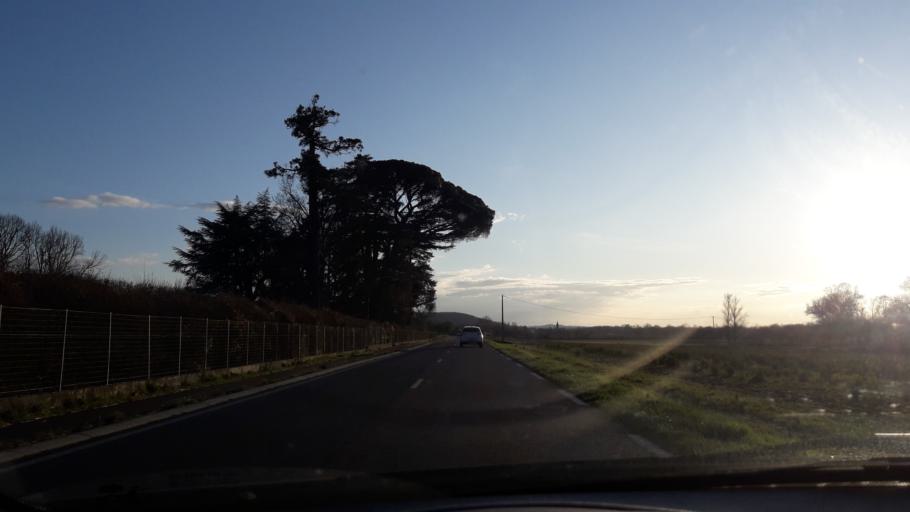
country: FR
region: Midi-Pyrenees
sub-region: Departement de la Haute-Garonne
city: Levignac
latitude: 43.6812
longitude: 1.2112
